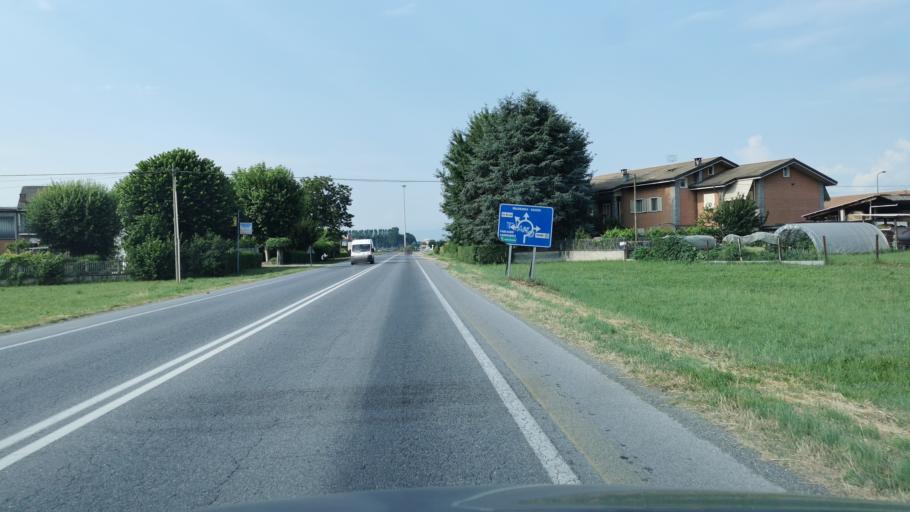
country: IT
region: Piedmont
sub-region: Provincia di Torino
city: Vigone
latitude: 44.8429
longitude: 7.5045
